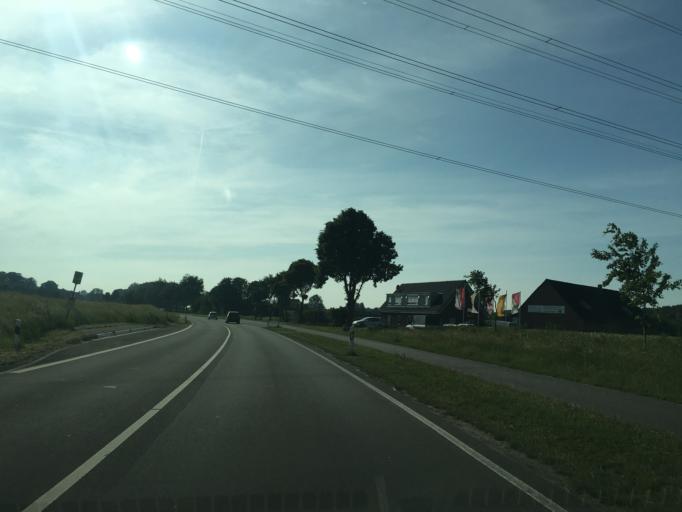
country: DE
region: North Rhine-Westphalia
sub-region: Regierungsbezirk Munster
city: Greven
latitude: 52.0964
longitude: 7.5769
